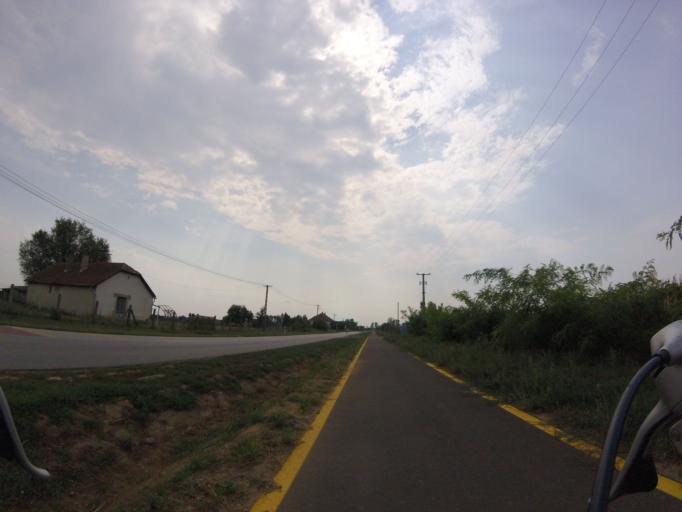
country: HU
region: Szabolcs-Szatmar-Bereg
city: Demecser
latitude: 48.0901
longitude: 21.9303
